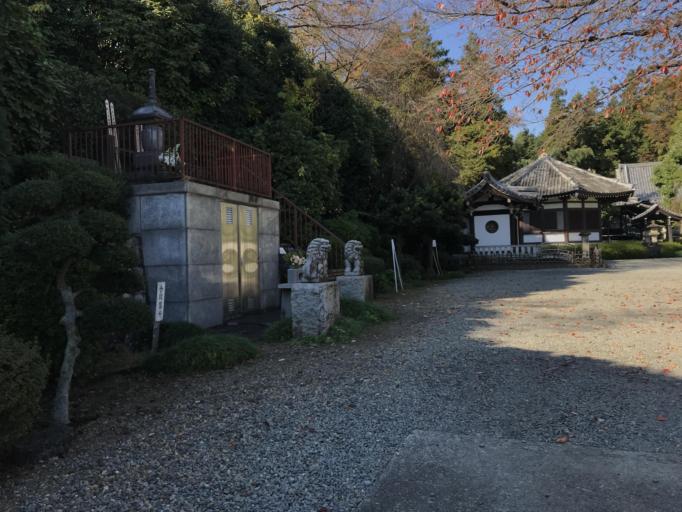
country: JP
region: Tokyo
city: Chofugaoka
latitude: 35.6031
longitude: 139.5454
